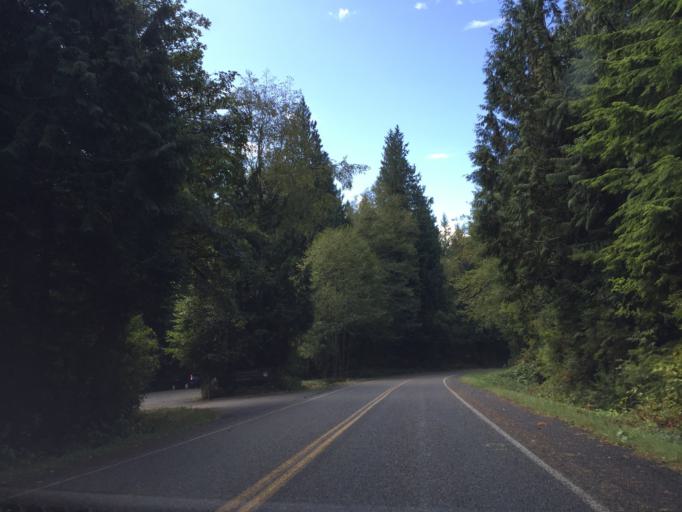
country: US
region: Washington
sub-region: Whatcom County
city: Sudden Valley
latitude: 48.7309
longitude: -122.3085
